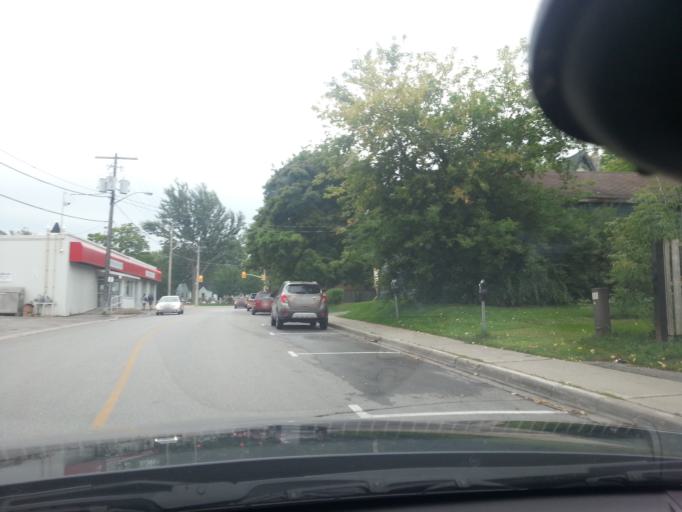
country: CA
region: Ontario
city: Picton
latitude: 44.0063
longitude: -77.1462
